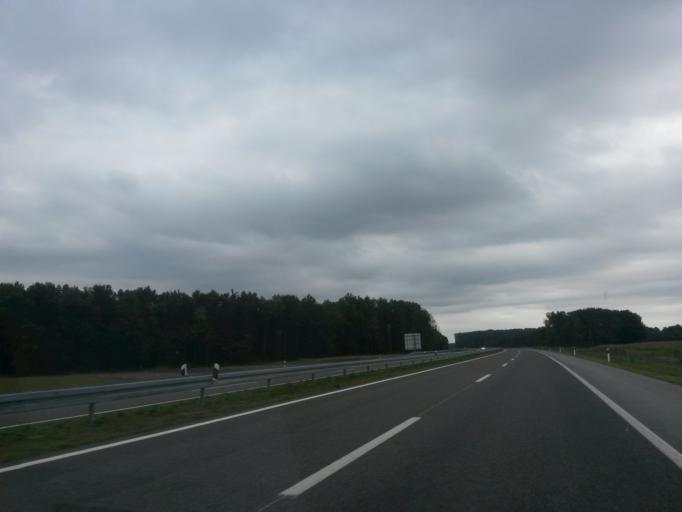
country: HR
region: Osjecko-Baranjska
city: Gorjani
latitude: 45.4110
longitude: 18.4377
